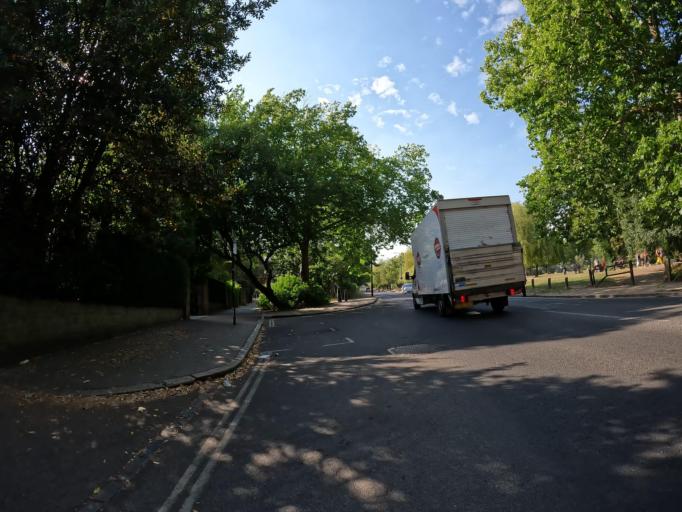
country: GB
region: England
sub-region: Greater London
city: Hadley Wood
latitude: 51.6609
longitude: -0.1735
